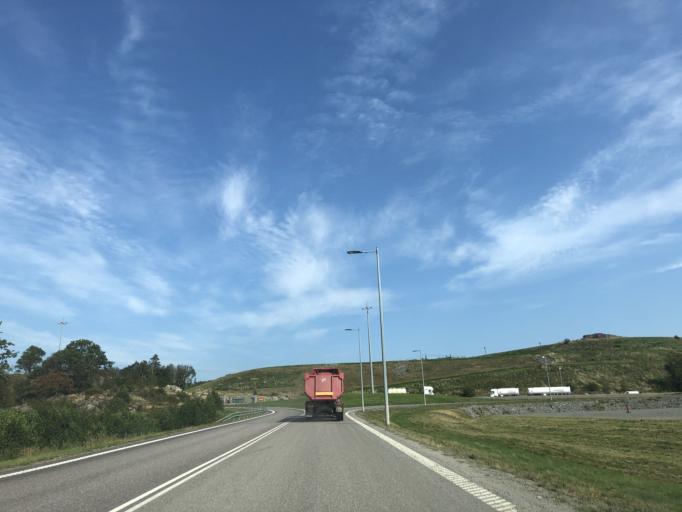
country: SE
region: Vaestra Goetaland
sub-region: Goteborg
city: Majorna
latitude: 57.7075
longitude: 11.8691
